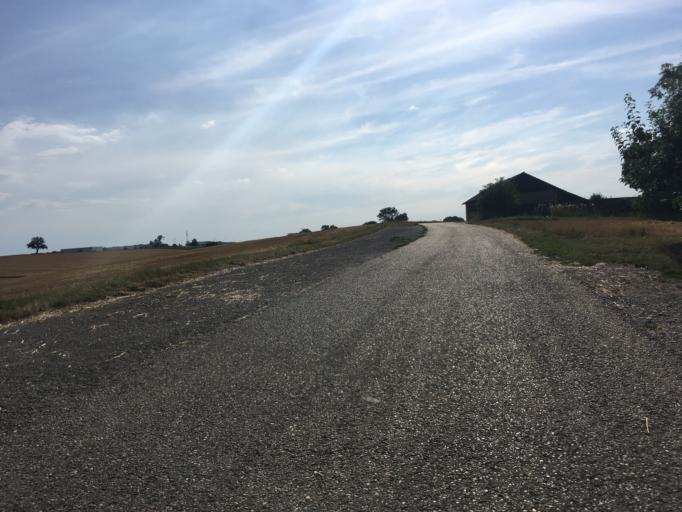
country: DE
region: Baden-Wuerttemberg
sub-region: Regierungsbezirk Stuttgart
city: Untereisesheim
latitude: 49.1963
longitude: 9.1895
